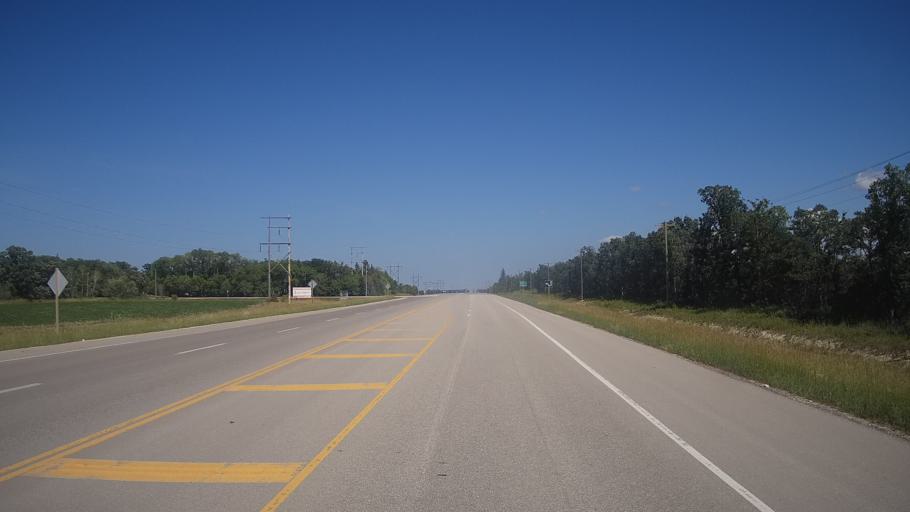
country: CA
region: Manitoba
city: Stonewall
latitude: 50.1228
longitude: -97.3364
